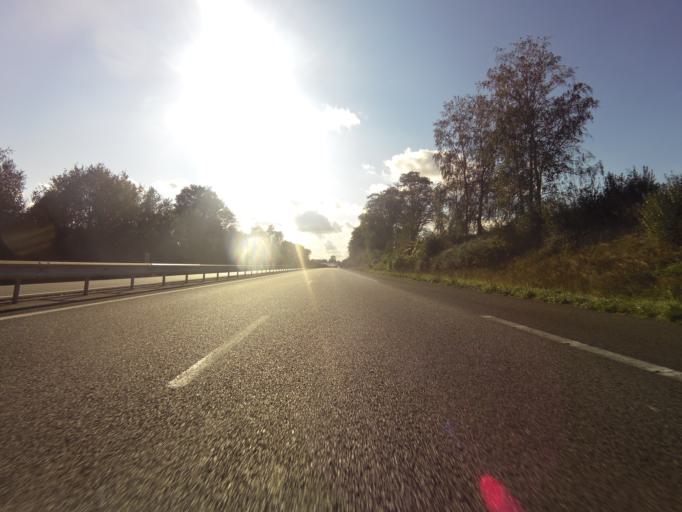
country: FR
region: Nord-Pas-de-Calais
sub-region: Departement du Pas-de-Calais
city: Bourlon
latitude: 50.1322
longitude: 3.1079
